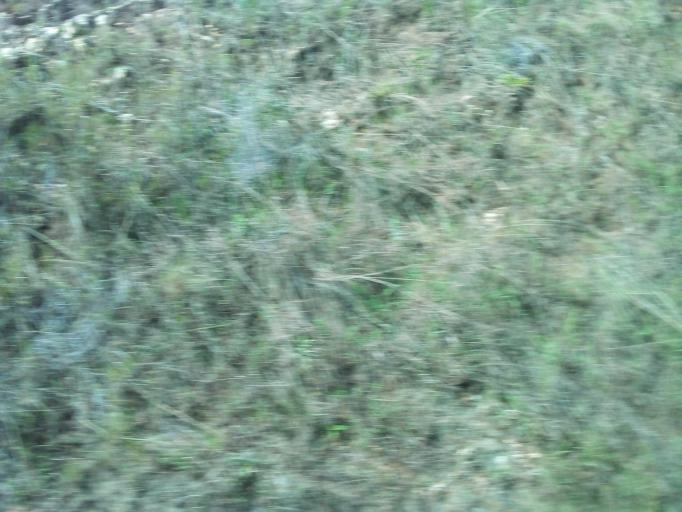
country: BR
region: Minas Gerais
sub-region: Caete
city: Caete
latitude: -19.8975
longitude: -43.7306
